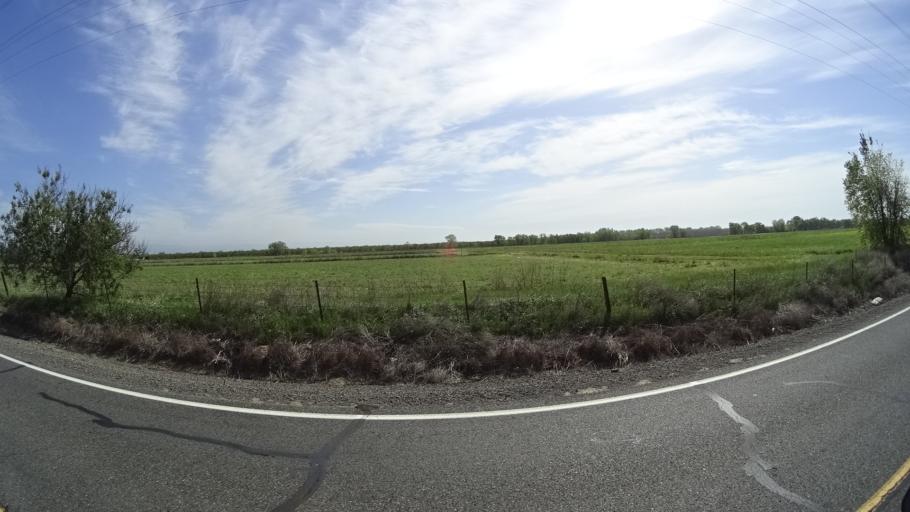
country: US
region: California
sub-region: Glenn County
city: Hamilton City
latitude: 39.6803
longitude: -122.0053
